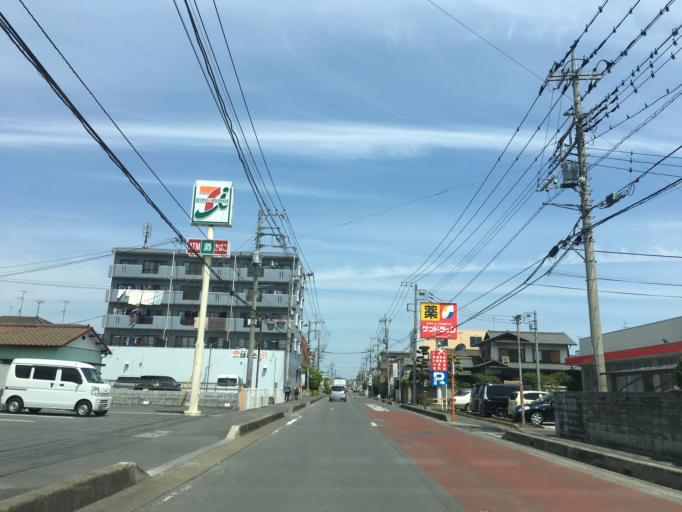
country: JP
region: Saitama
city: Okegawa
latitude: 35.9564
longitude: 139.5650
